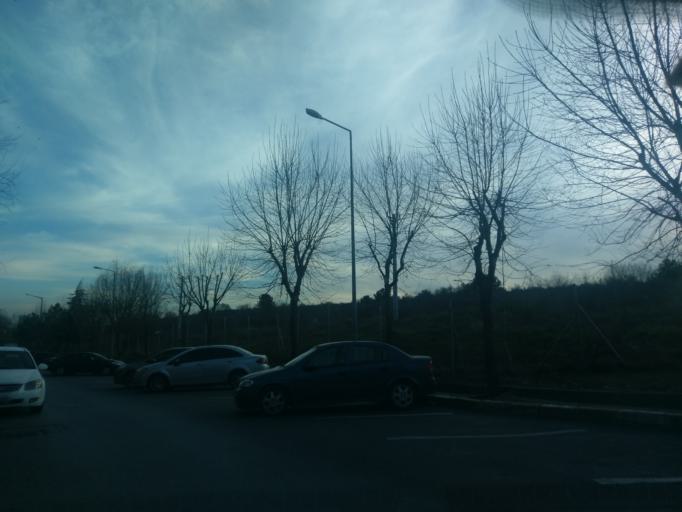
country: TR
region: Istanbul
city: Mahmutbey
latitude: 41.0378
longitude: 28.7618
